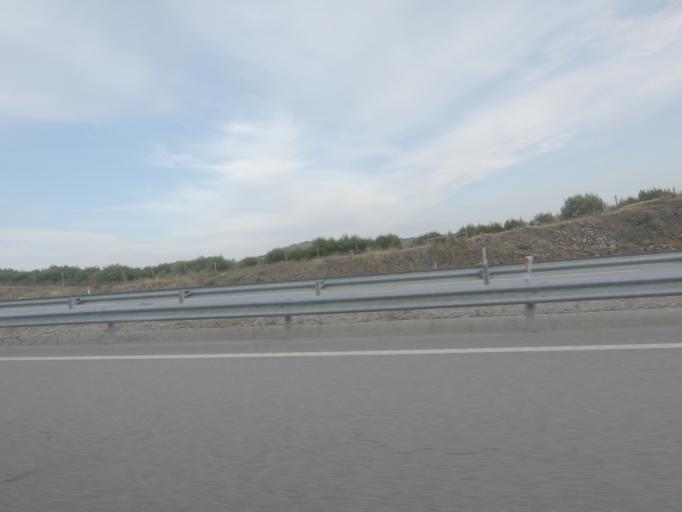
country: PT
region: Vila Real
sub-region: Vila Real
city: Vila Real
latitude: 41.3836
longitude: -7.6640
